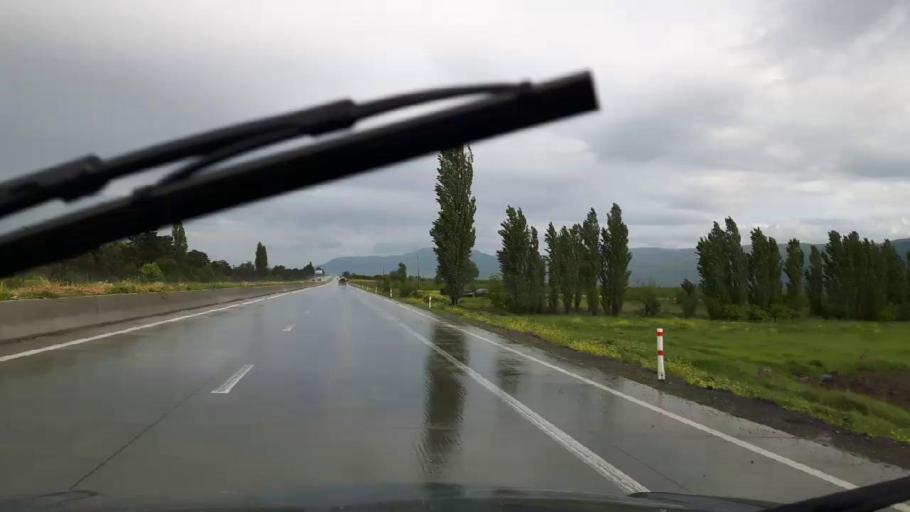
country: GE
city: Agara
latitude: 42.0444
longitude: 43.9221
